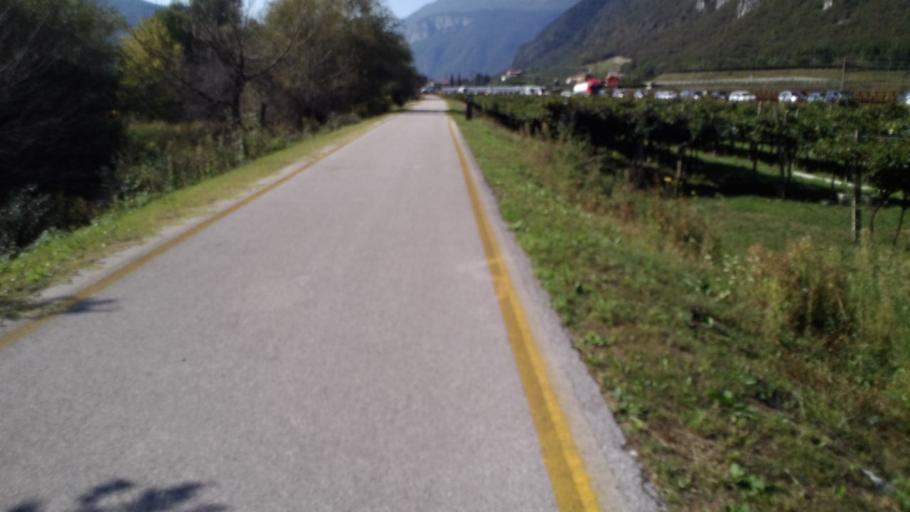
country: IT
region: Trentino-Alto Adige
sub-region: Provincia di Trento
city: Avio
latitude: 45.7136
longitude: 10.9311
